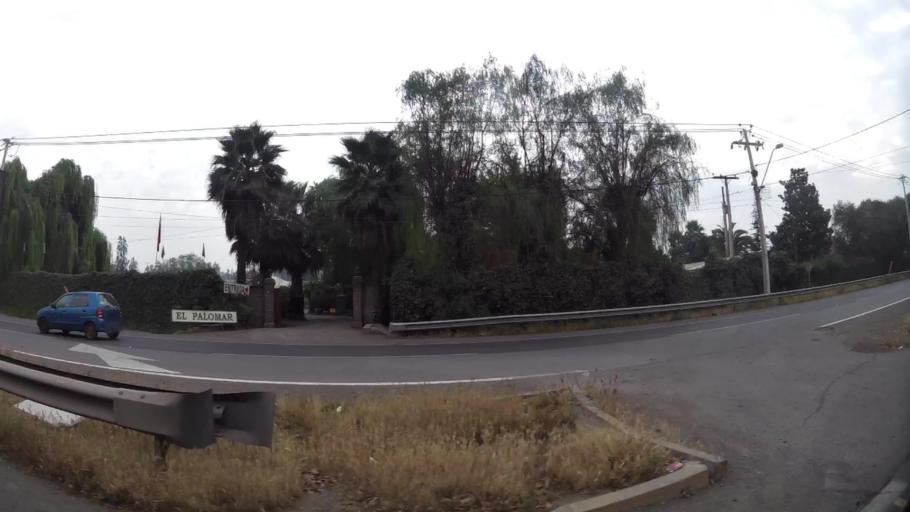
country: CL
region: Santiago Metropolitan
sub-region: Provincia de Chacabuco
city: Chicureo Abajo
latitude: -33.2417
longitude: -70.7000
